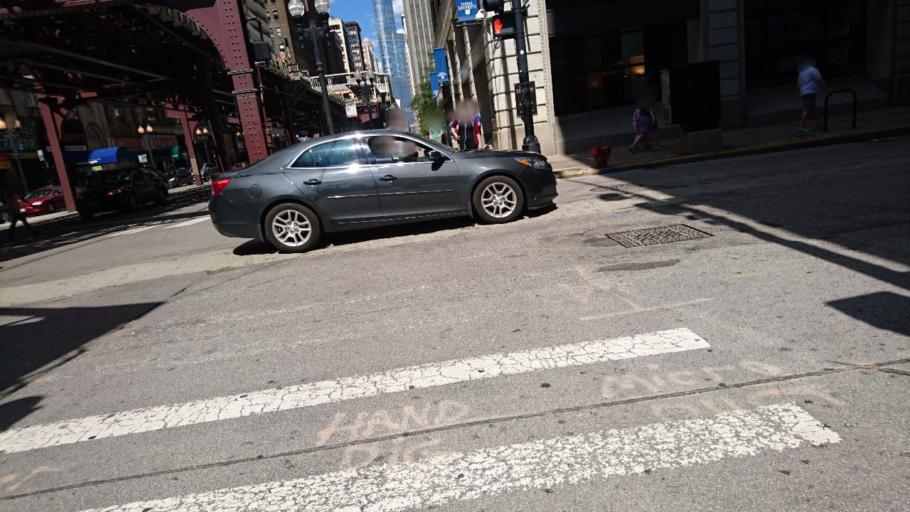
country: US
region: Illinois
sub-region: Cook County
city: Chicago
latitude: 41.8781
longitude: -87.6259
